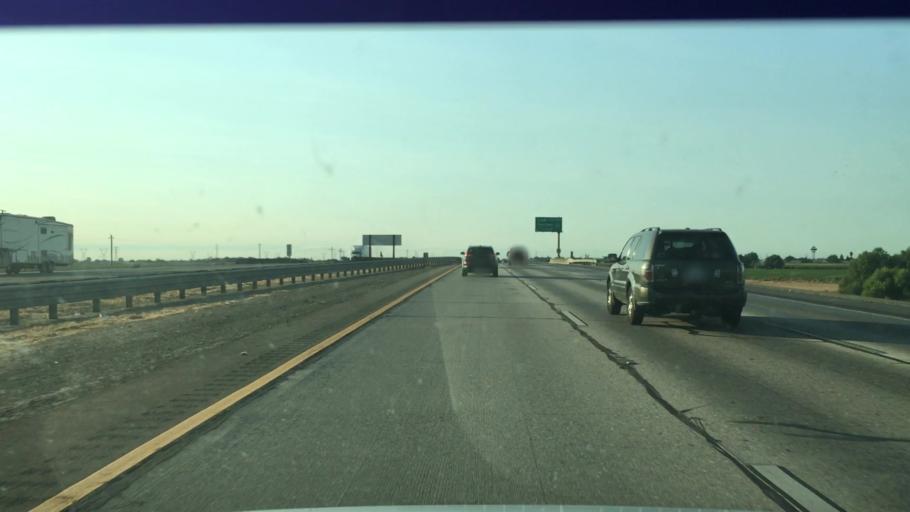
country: US
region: California
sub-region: San Joaquin County
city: Woodbridge
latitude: 38.0952
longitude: -121.3858
